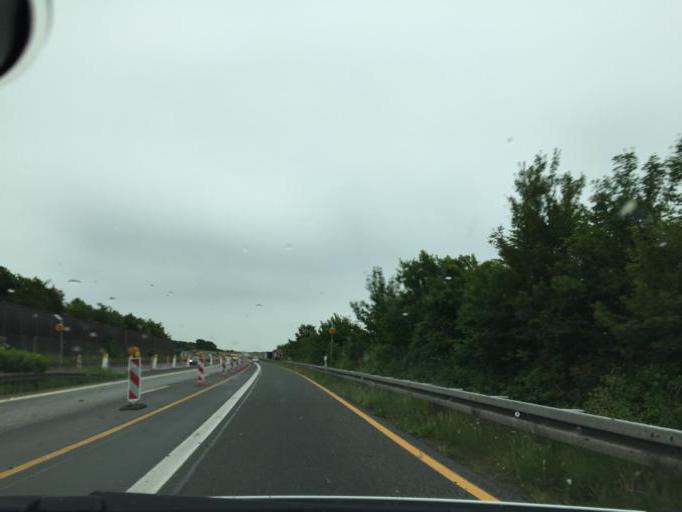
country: DE
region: Bavaria
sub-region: Regierungsbezirk Unterfranken
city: Gadheim
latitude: 50.0092
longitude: 10.3547
